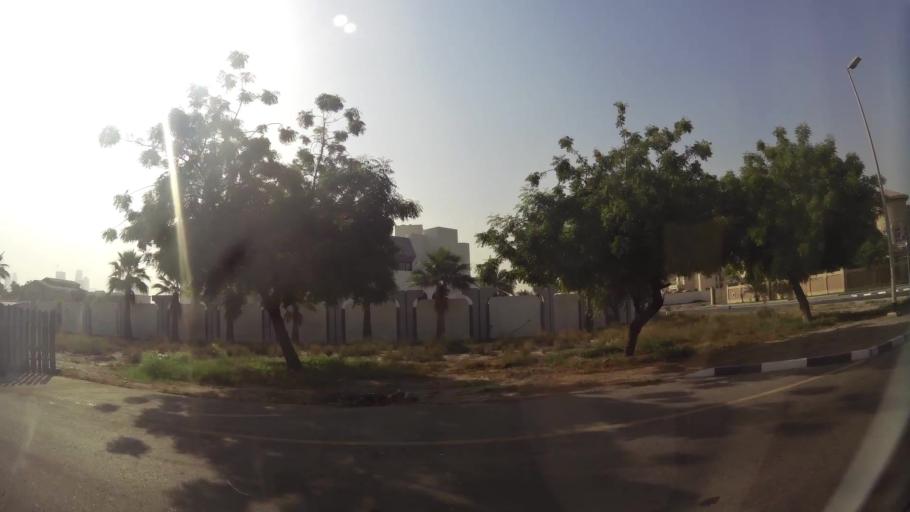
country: AE
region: Ash Shariqah
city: Sharjah
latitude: 25.3097
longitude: 55.3415
